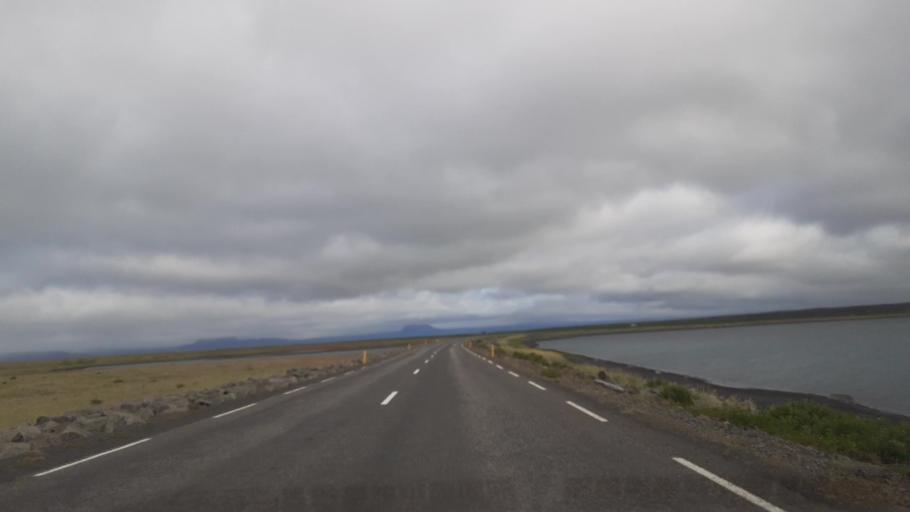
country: IS
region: Northeast
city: Husavik
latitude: 66.1212
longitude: -16.9325
